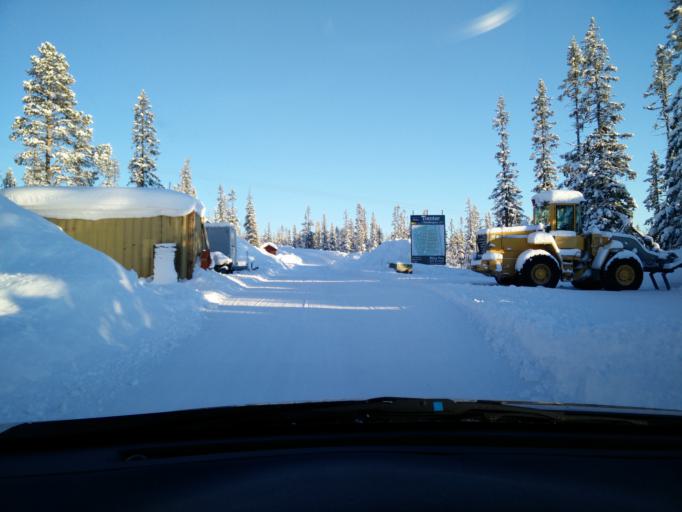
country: SE
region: Jaemtland
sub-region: Bergs Kommun
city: Hoverberg
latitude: 62.4964
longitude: 14.1213
